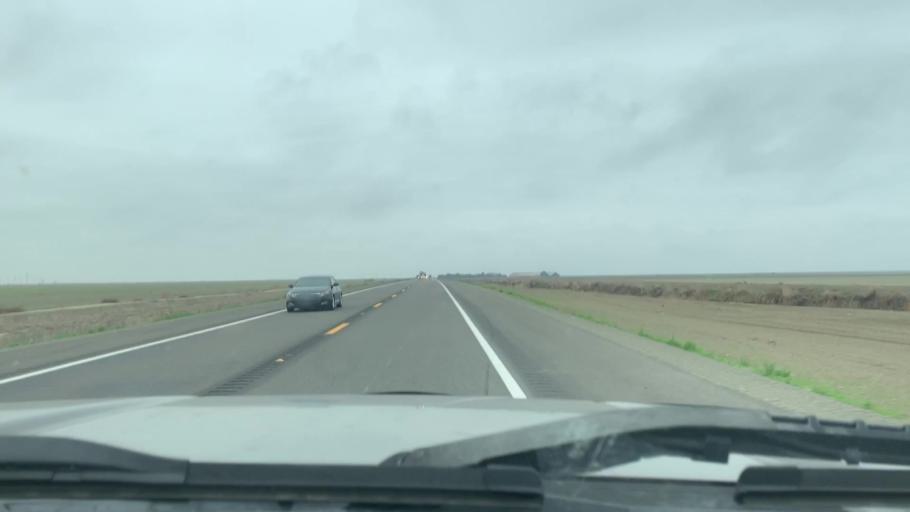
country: US
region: California
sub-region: Kings County
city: Kettleman City
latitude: 36.0399
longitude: -119.9565
